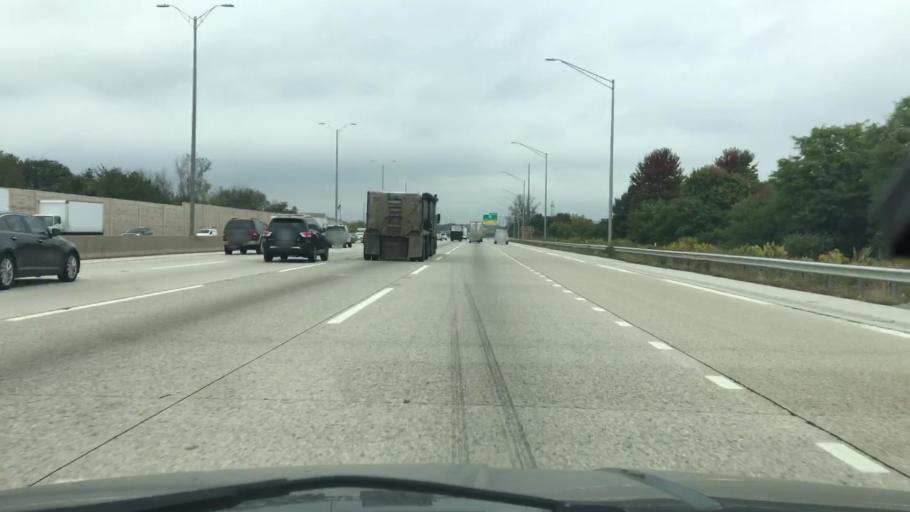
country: US
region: Illinois
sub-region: Lake County
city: Bannockburn
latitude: 42.1921
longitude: -87.8821
